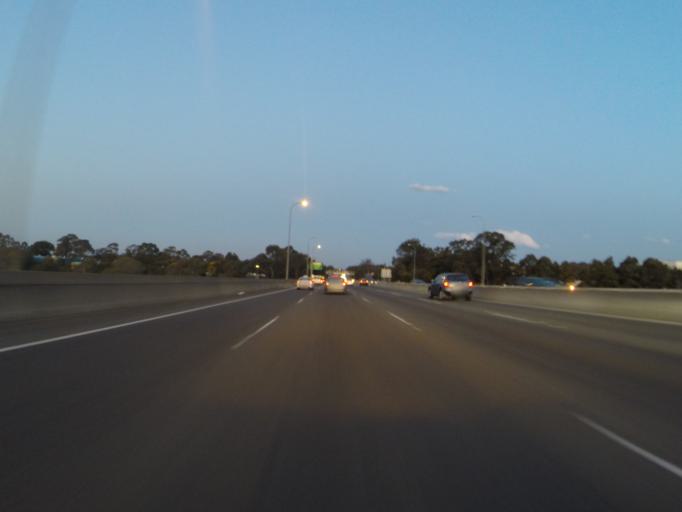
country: AU
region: New South Wales
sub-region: Campbelltown Municipality
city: Glenfield
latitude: -33.9390
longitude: 150.9193
